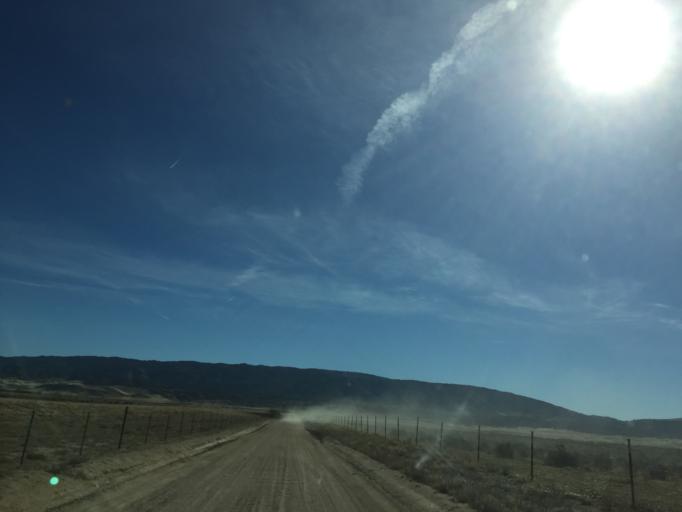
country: US
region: California
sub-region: Kern County
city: Lebec
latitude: 34.8211
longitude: -118.6609
